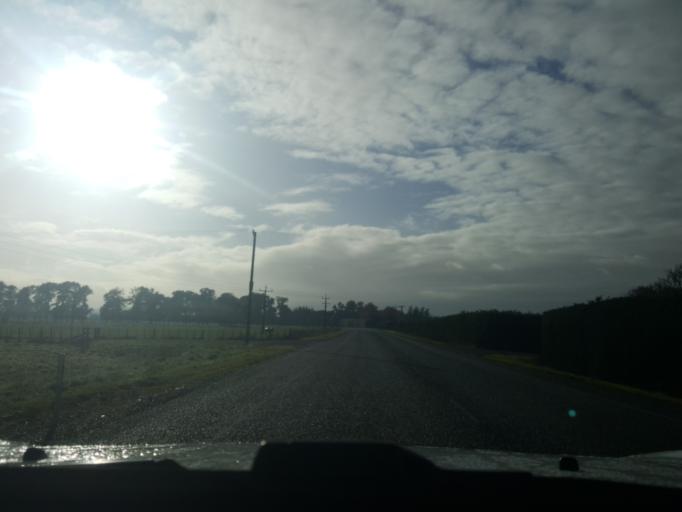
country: NZ
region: Waikato
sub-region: Waipa District
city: Cambridge
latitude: -37.7800
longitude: 175.3967
